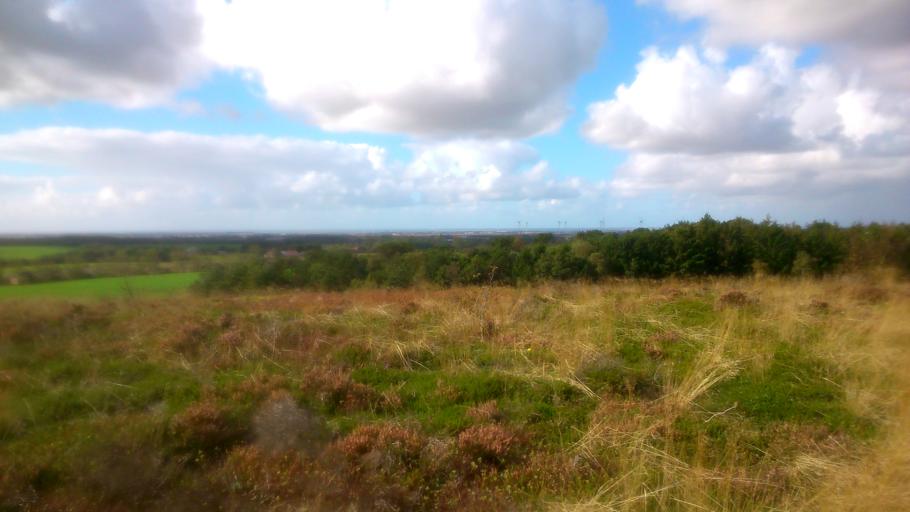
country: DK
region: Central Jutland
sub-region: Ringkobing-Skjern Kommune
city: Skjern
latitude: 56.0455
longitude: 8.4436
